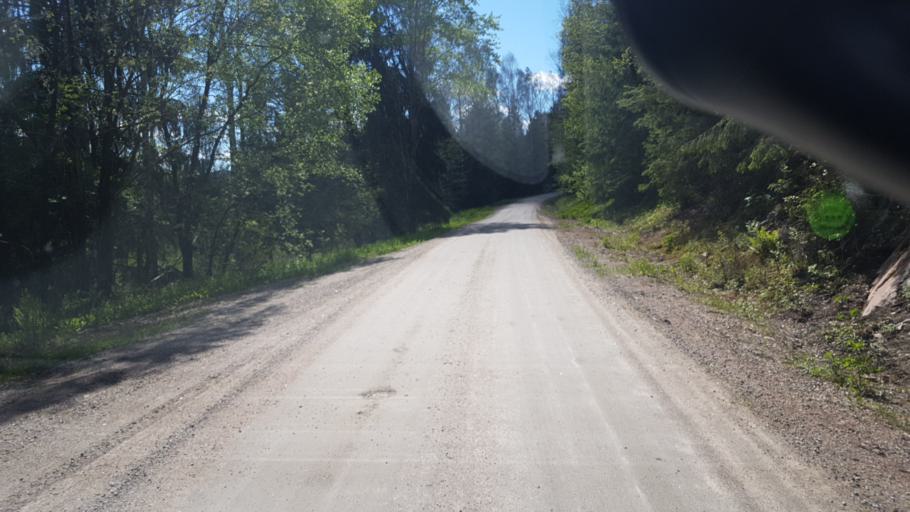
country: SE
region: Vaermland
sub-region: Arvika Kommun
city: Arvika
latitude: 59.6815
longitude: 12.7707
